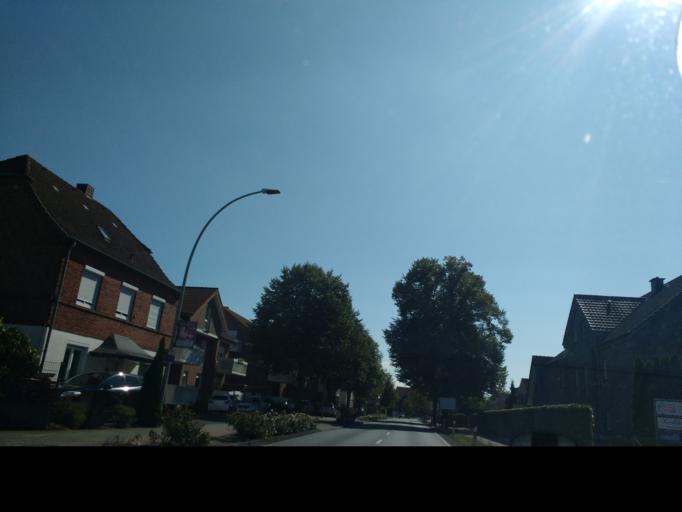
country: DE
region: North Rhine-Westphalia
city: Rietberg
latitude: 51.8128
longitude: 8.4246
